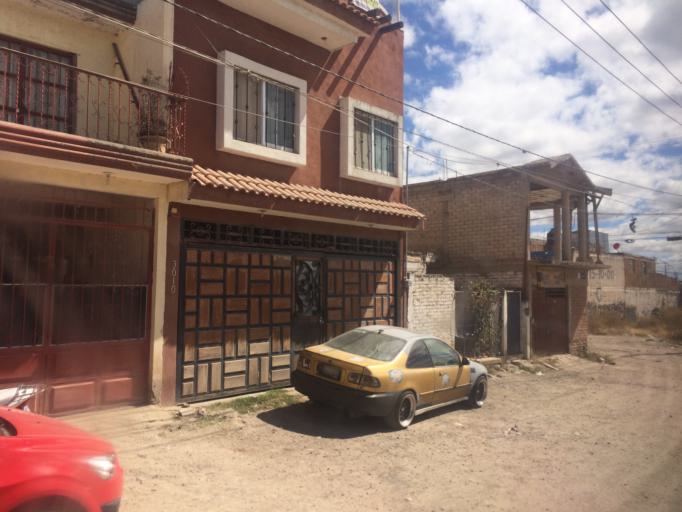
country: MX
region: Guanajuato
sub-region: Leon
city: La Ermita
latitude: 21.1499
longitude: -101.7364
